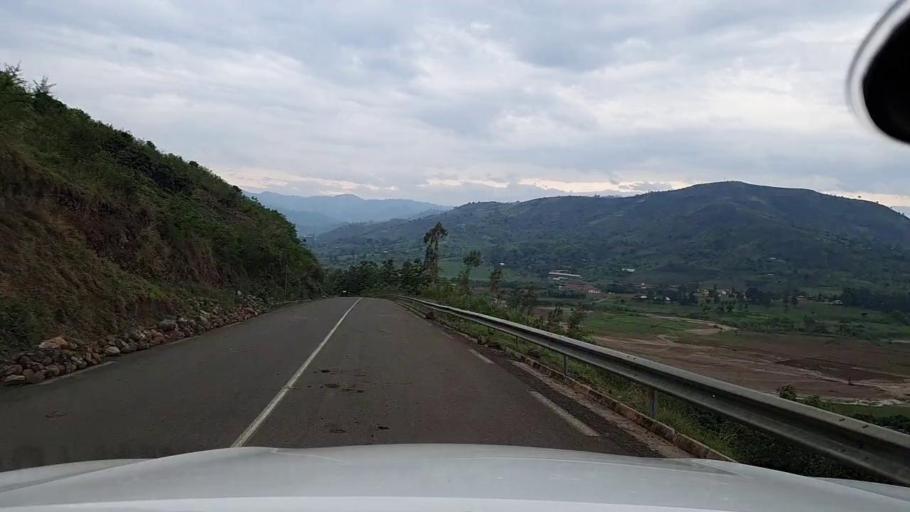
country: BI
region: Cibitoke
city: Cibitoke
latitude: -2.7352
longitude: 29.0373
